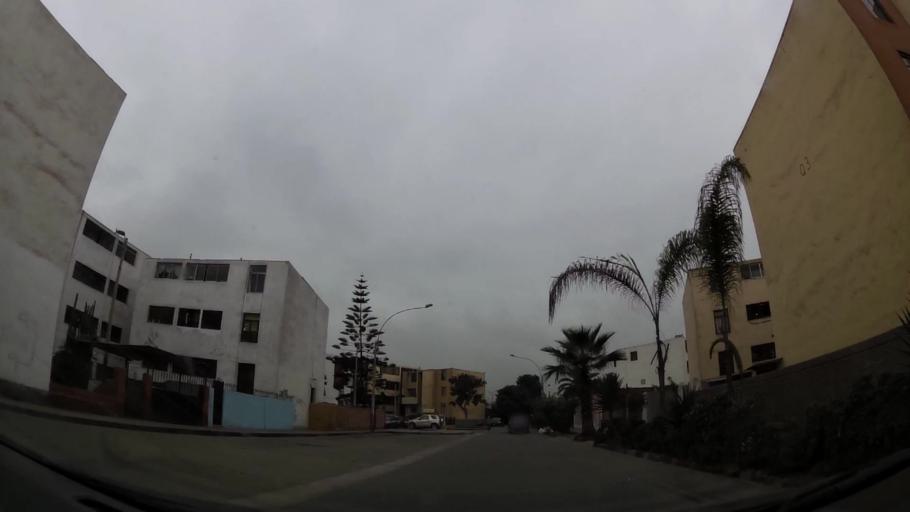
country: PE
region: Callao
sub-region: Callao
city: Callao
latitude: -12.0609
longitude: -77.0735
